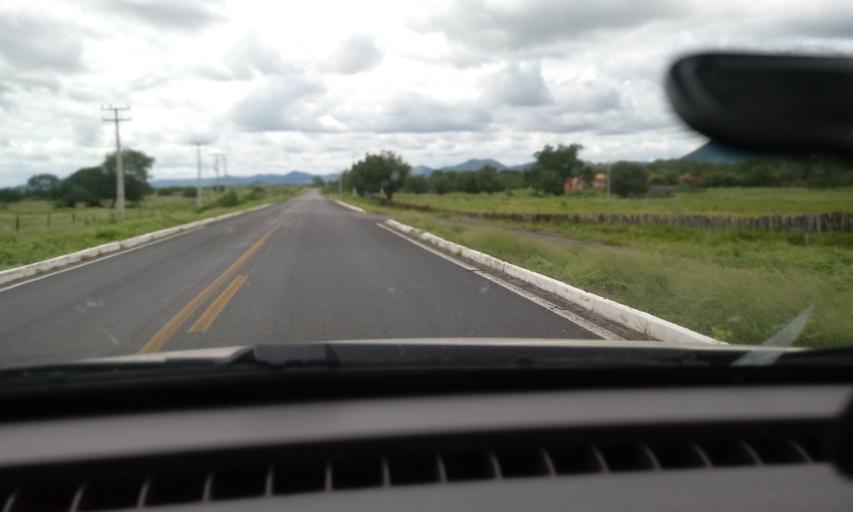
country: BR
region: Bahia
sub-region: Guanambi
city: Guanambi
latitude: -13.9536
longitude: -42.8547
